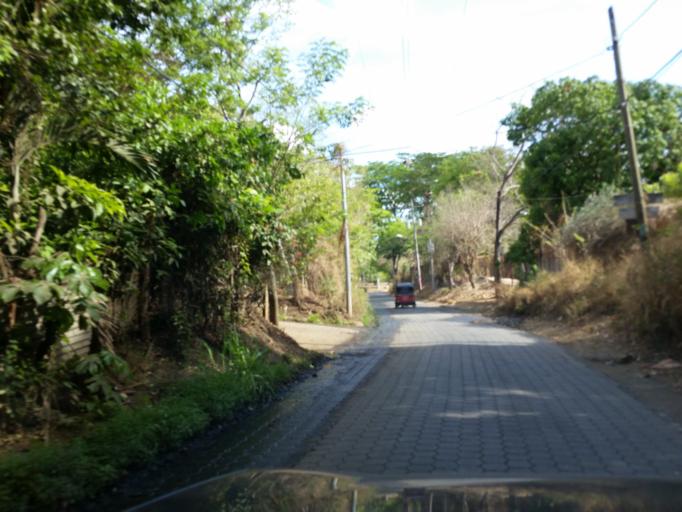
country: NI
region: Managua
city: Managua
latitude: 12.0798
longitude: -86.2273
